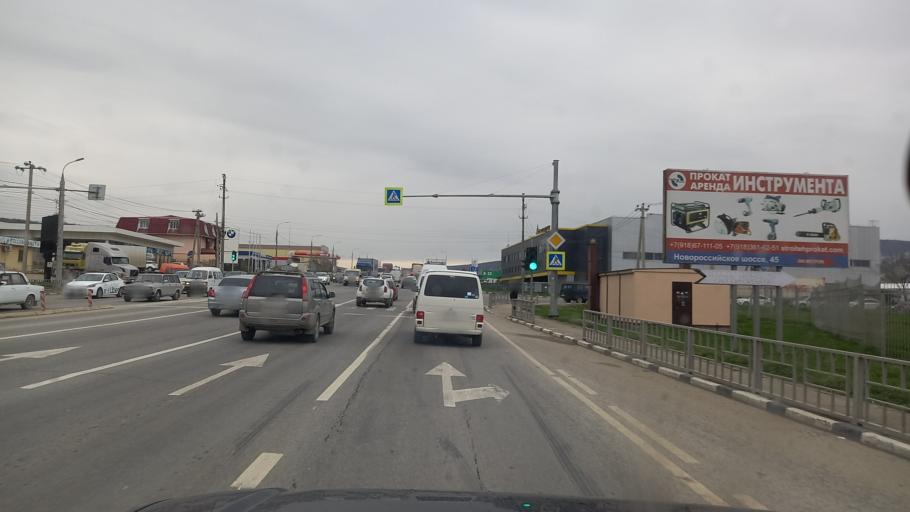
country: RU
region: Krasnodarskiy
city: Gayduk
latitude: 44.7715
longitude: 37.6965
